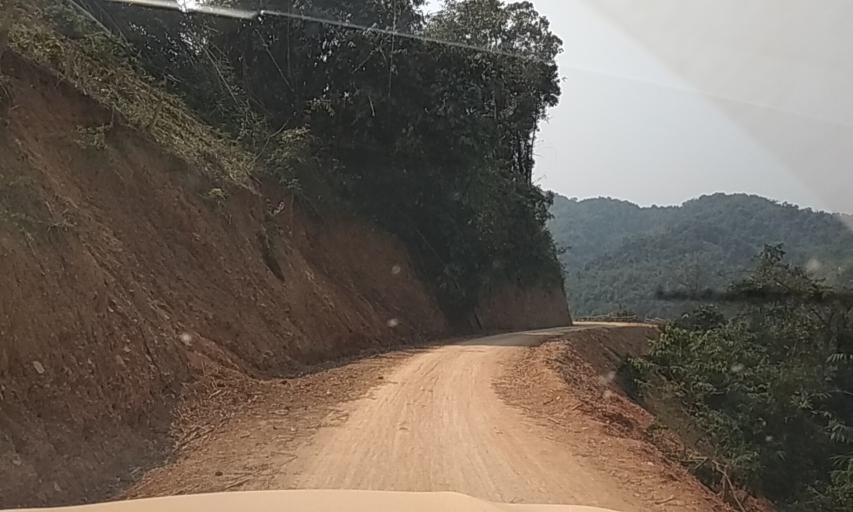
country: LA
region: Phongsali
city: Phongsali
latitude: 21.4740
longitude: 102.4338
